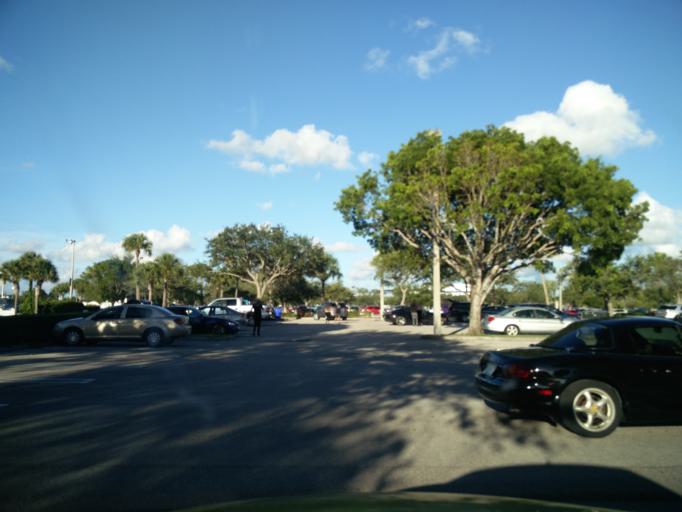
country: US
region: Florida
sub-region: Palm Beach County
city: Royal Palm Beach
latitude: 26.6862
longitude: -80.1915
